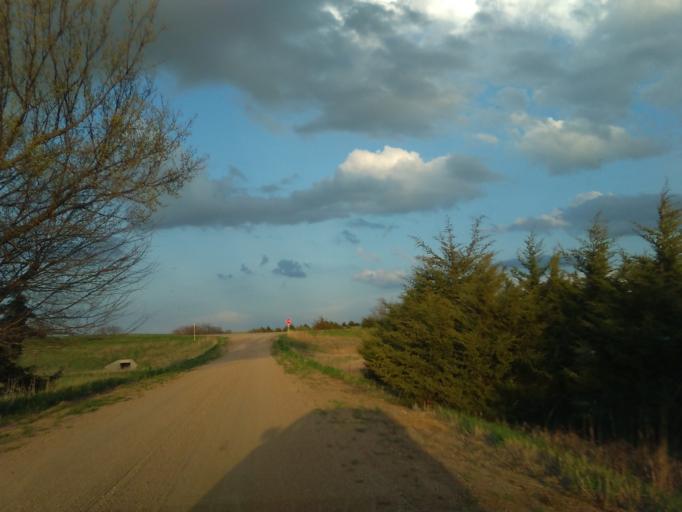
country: US
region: Nebraska
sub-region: Webster County
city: Red Cloud
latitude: 40.2198
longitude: -98.3320
